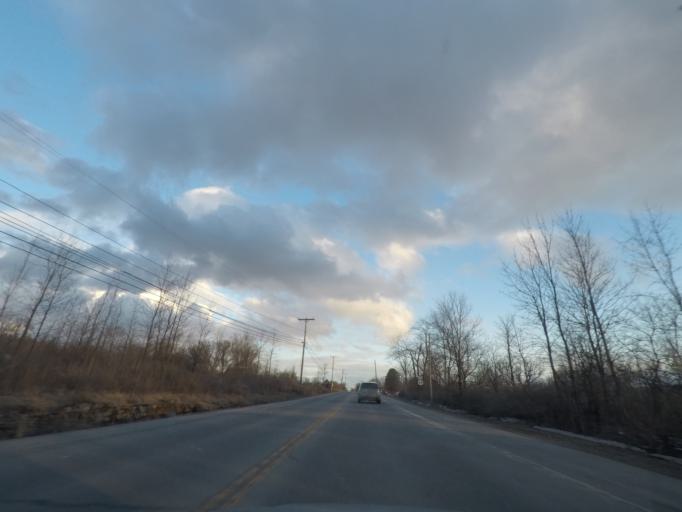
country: US
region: New York
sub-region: Montgomery County
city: Saint Johnsville
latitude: 42.9922
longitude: -74.6566
